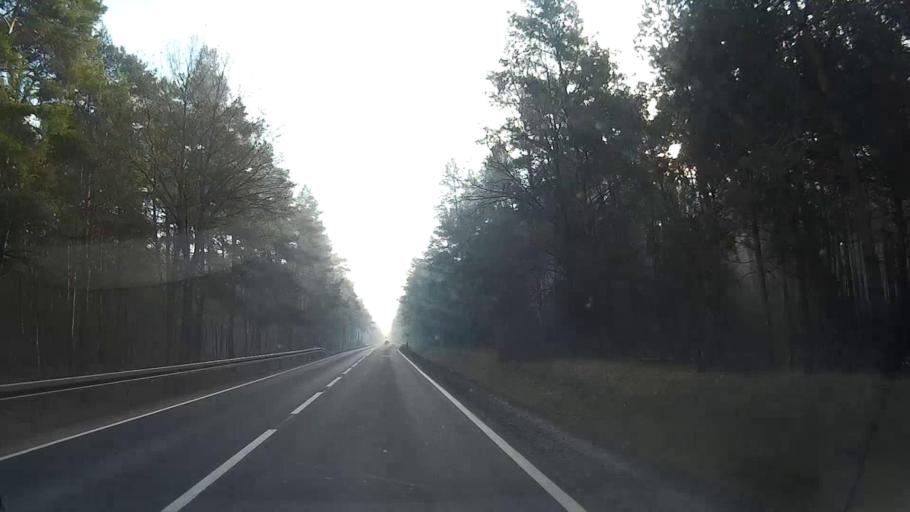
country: PL
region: Lesser Poland Voivodeship
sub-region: Powiat chrzanowski
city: Zarki
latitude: 50.0806
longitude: 19.3721
